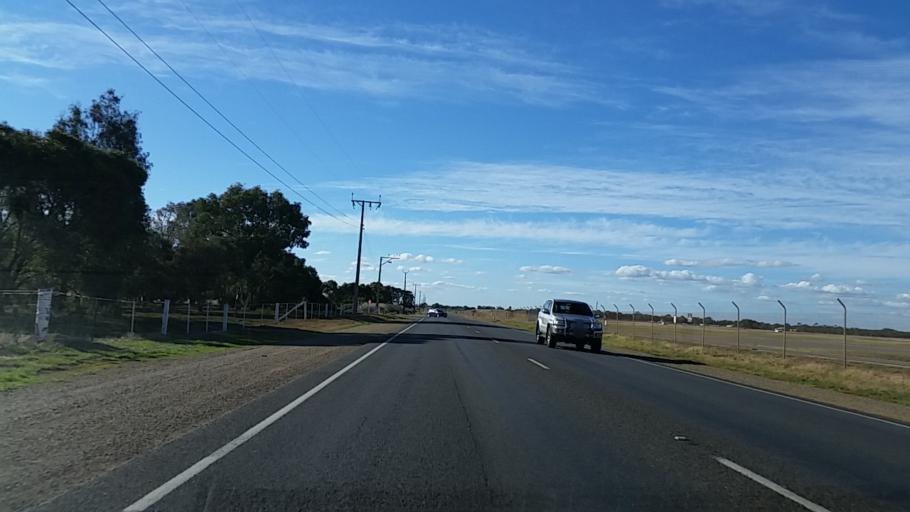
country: AU
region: South Australia
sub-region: Playford
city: Virginia
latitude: -34.7025
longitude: 138.6096
